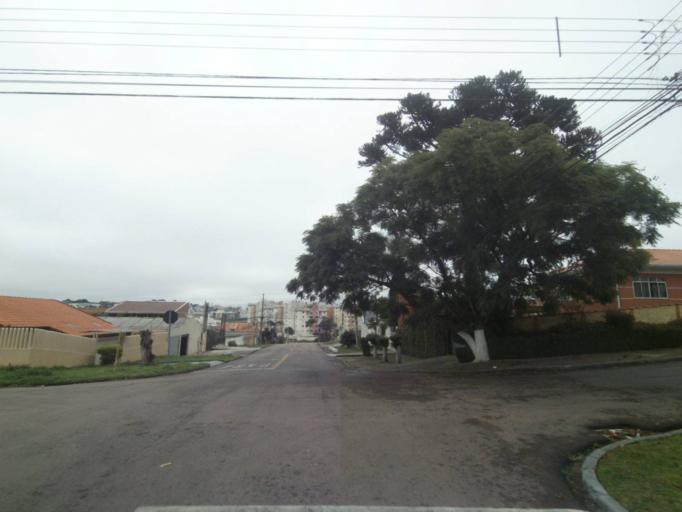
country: BR
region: Parana
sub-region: Curitiba
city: Curitiba
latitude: -25.5042
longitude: -49.3056
